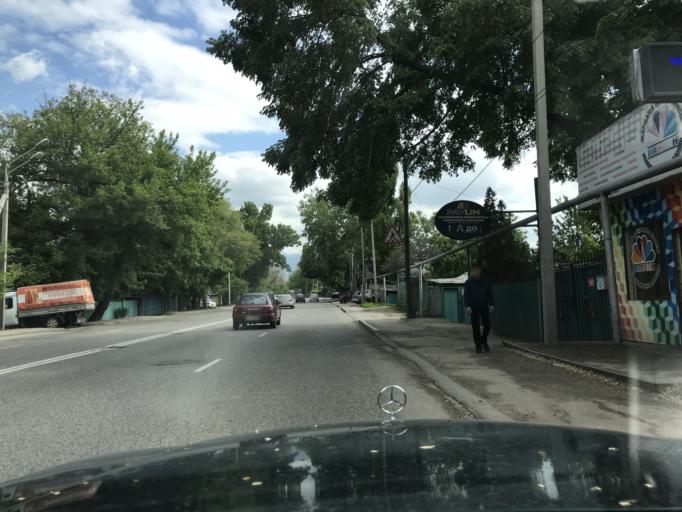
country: KZ
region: Almaty Qalasy
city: Almaty
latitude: 43.2897
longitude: 76.9013
